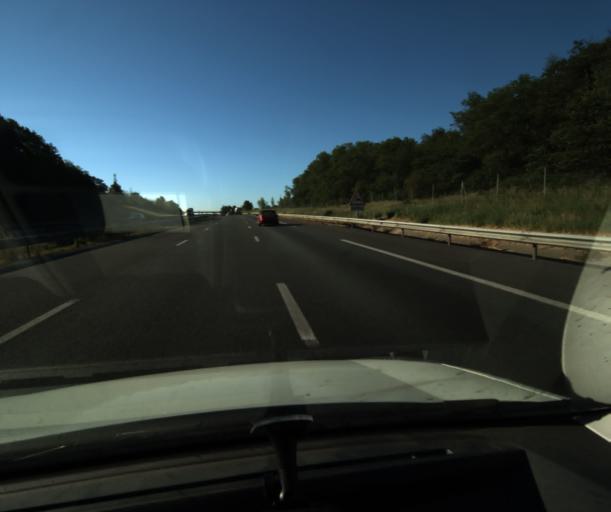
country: FR
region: Midi-Pyrenees
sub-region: Departement de la Haute-Garonne
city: Castelnau-d'Estretefonds
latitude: 43.8020
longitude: 1.3689
